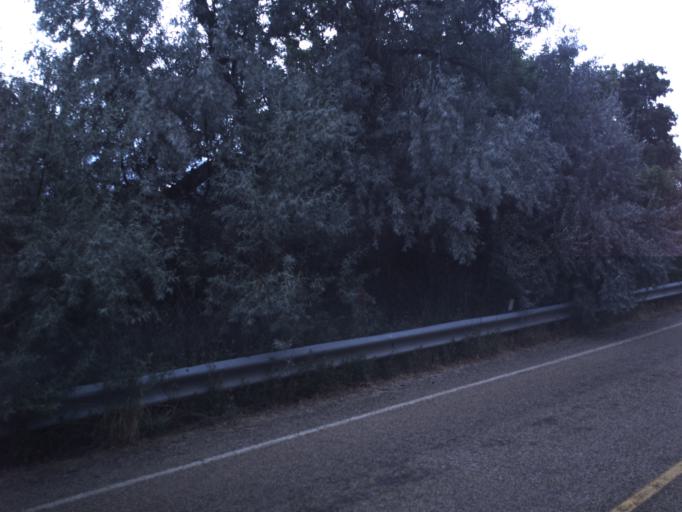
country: US
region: Utah
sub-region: Weber County
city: Riverdale
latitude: 41.1541
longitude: -112.0000
